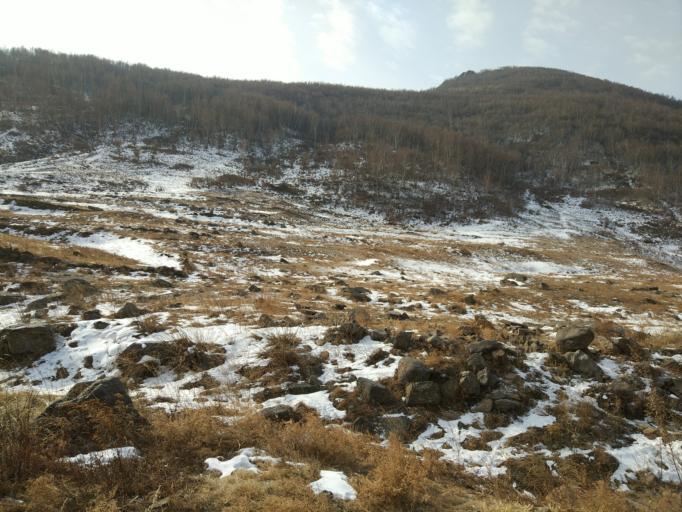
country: CN
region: Hebei
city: Xiwanzi
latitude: 40.8538
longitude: 115.4622
